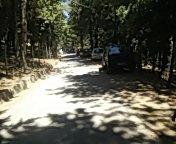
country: IT
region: Sicily
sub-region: Palermo
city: Castelbuono
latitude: 37.9014
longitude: 14.0891
